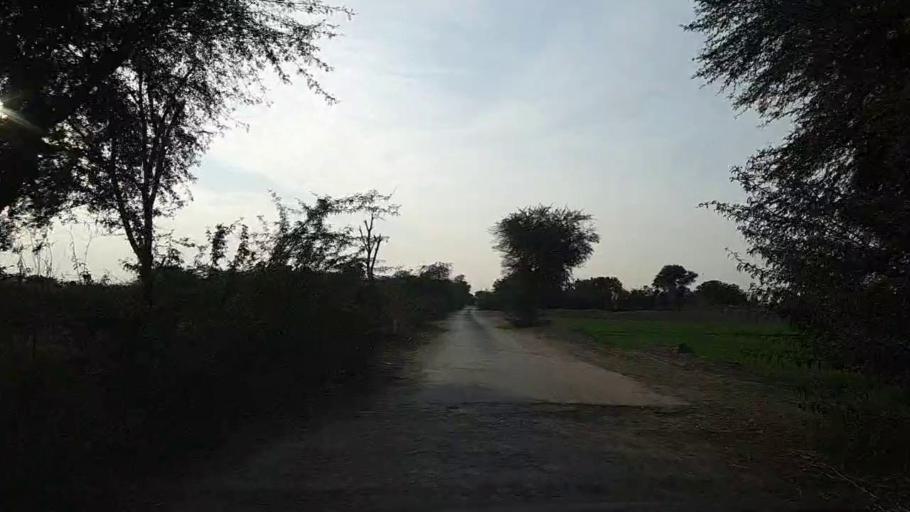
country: PK
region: Sindh
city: Jam Sahib
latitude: 26.4318
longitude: 68.5694
